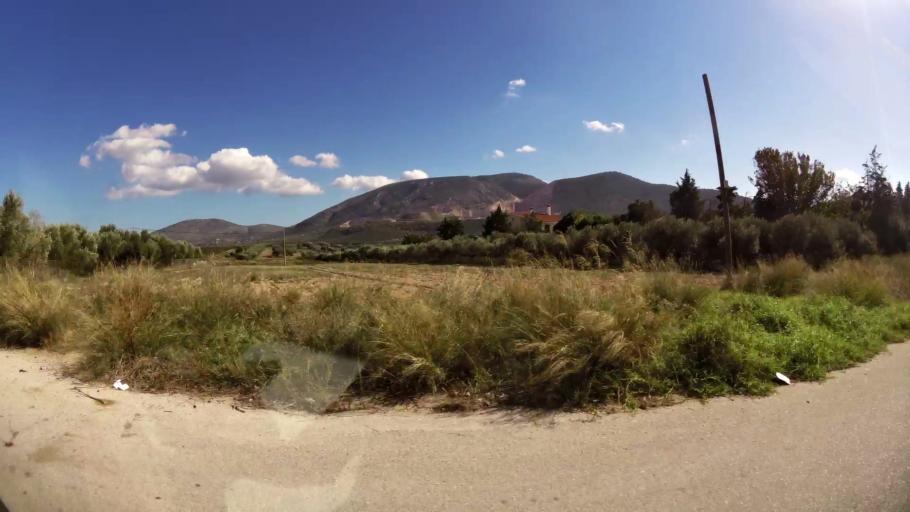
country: GR
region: Attica
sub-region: Nomarchia Anatolikis Attikis
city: Markopoulo
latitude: 37.8742
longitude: 23.9341
